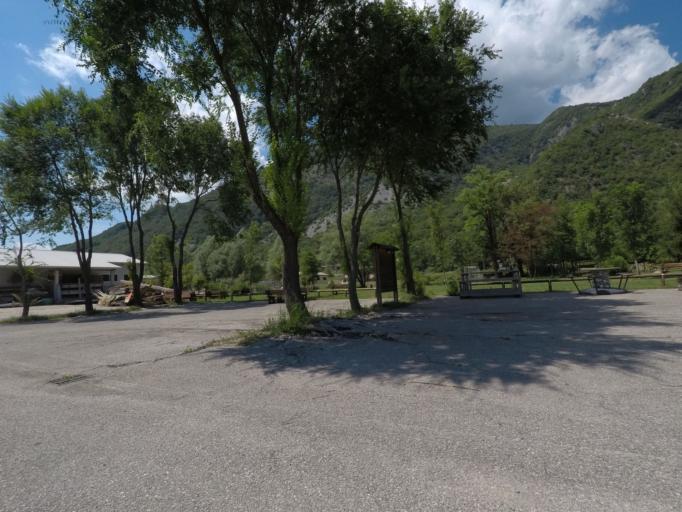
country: IT
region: Friuli Venezia Giulia
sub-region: Provincia di Udine
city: Forgaria nel Friuli
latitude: 46.2250
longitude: 13.0202
